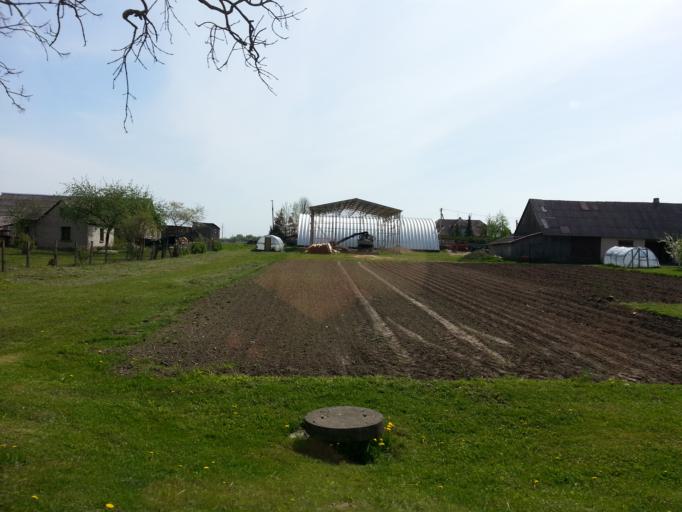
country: LT
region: Panevezys
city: Pasvalys
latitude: 55.9263
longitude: 24.2380
